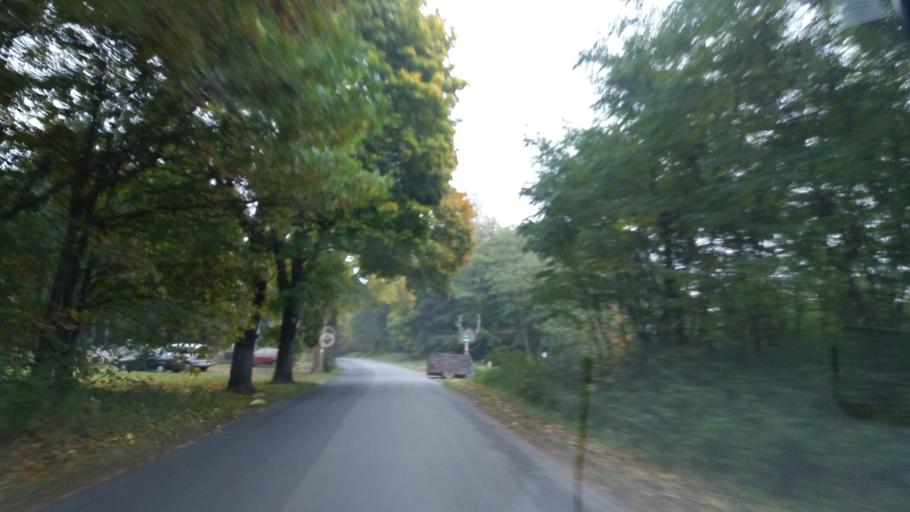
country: PL
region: Lubusz
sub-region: Powiat strzelecko-drezdenecki
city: Dobiegniew
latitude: 53.0569
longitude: 15.7587
